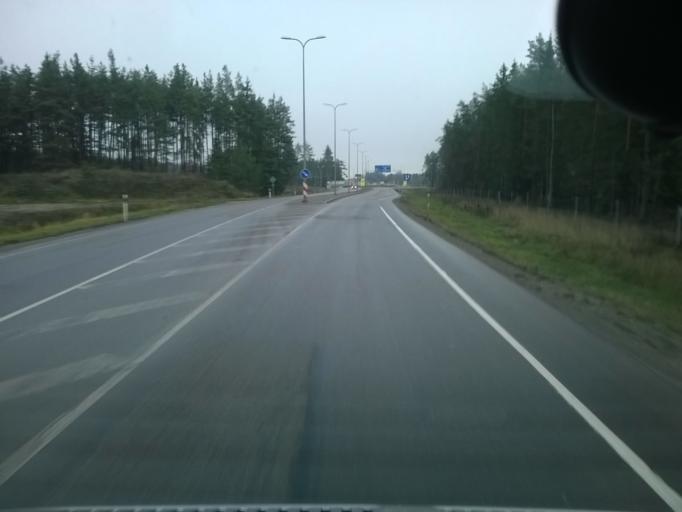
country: EE
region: Harju
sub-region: Kiili vald
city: Kiili
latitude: 59.3168
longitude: 24.7581
